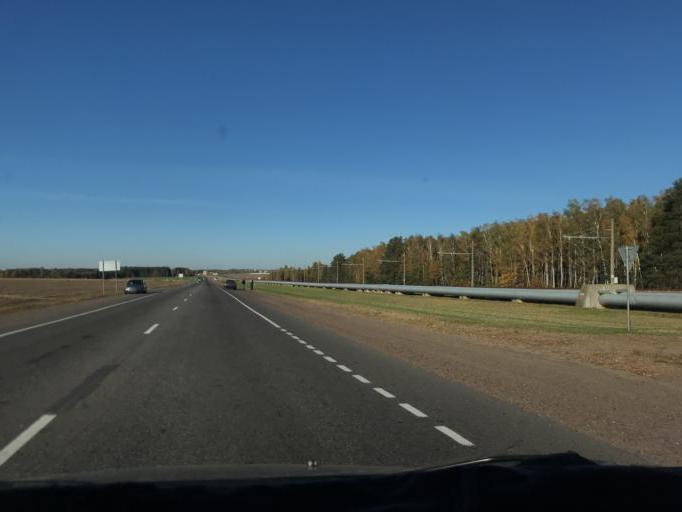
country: BY
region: Gomel
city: Mazyr
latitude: 51.9812
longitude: 29.2601
